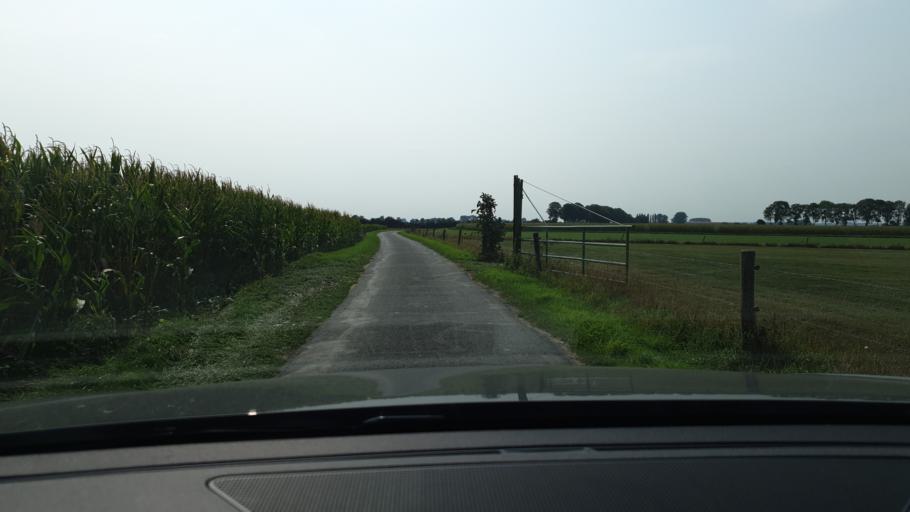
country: NL
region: Gelderland
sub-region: Gemeente Zevenaar
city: Zevenaar
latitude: 51.8559
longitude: 6.0601
